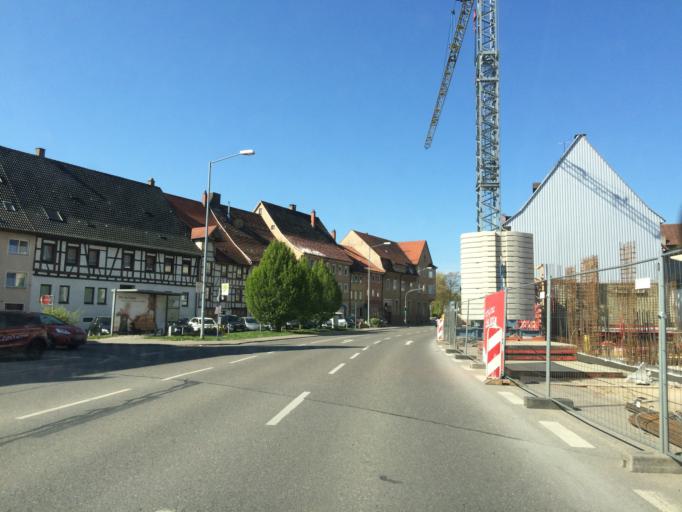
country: DE
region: Baden-Wuerttemberg
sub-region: Freiburg Region
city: Tuttlingen
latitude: 47.9877
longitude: 8.8213
